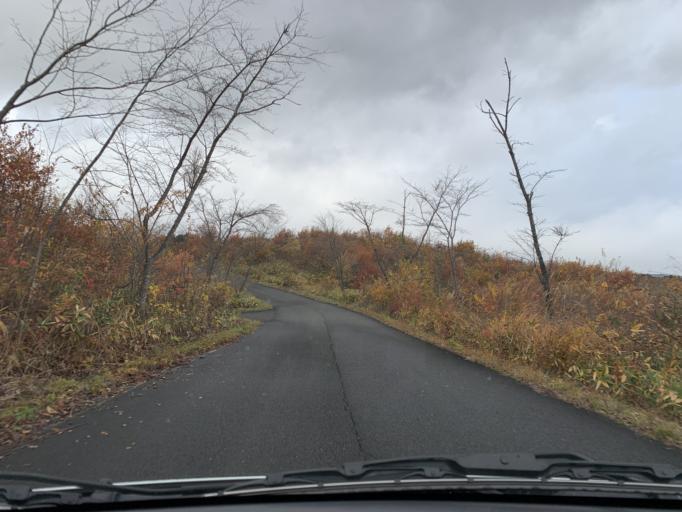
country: JP
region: Iwate
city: Mizusawa
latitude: 39.0798
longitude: 141.0230
